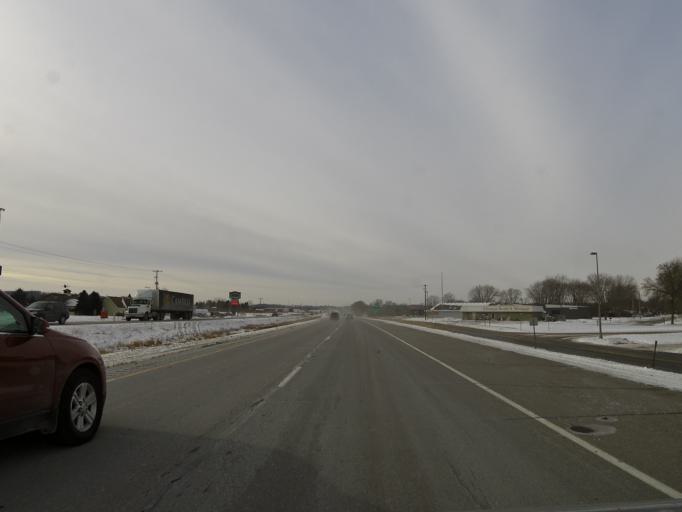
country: US
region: Minnesota
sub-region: Scott County
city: Belle Plaine
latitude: 44.6168
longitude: -93.7629
